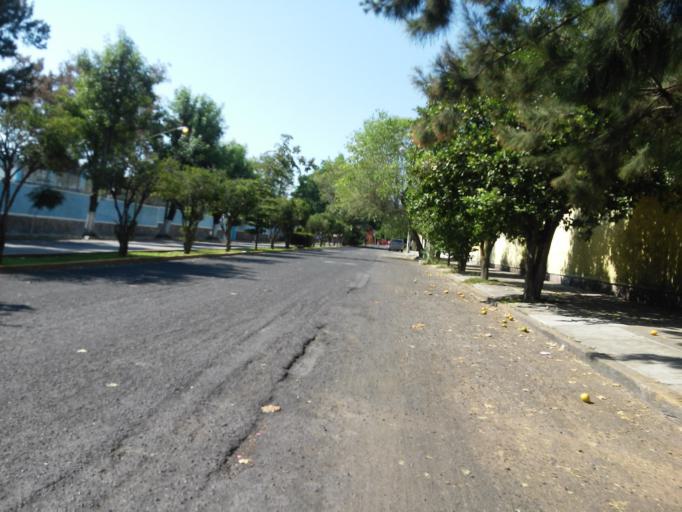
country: MX
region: Jalisco
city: Guadalajara
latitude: 20.6585
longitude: -103.3916
